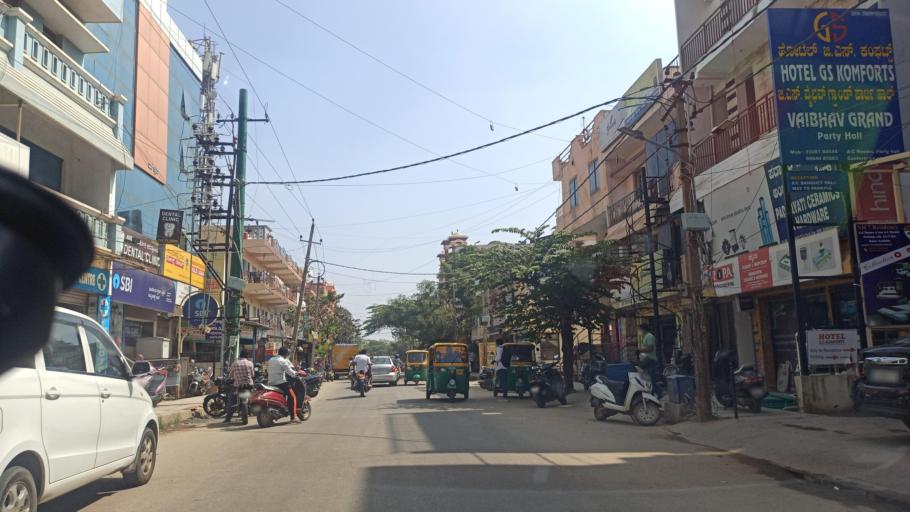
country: IN
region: Karnataka
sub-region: Bangalore Urban
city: Yelahanka
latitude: 13.0666
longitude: 77.5962
